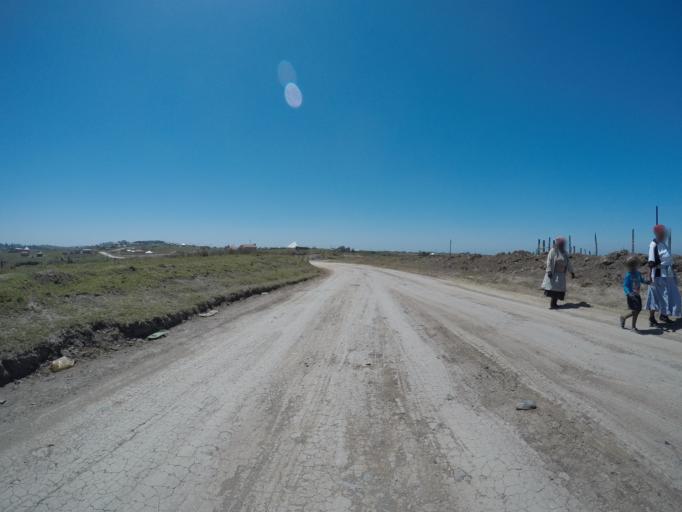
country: ZA
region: Eastern Cape
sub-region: OR Tambo District Municipality
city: Libode
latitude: -31.9446
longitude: 29.0270
